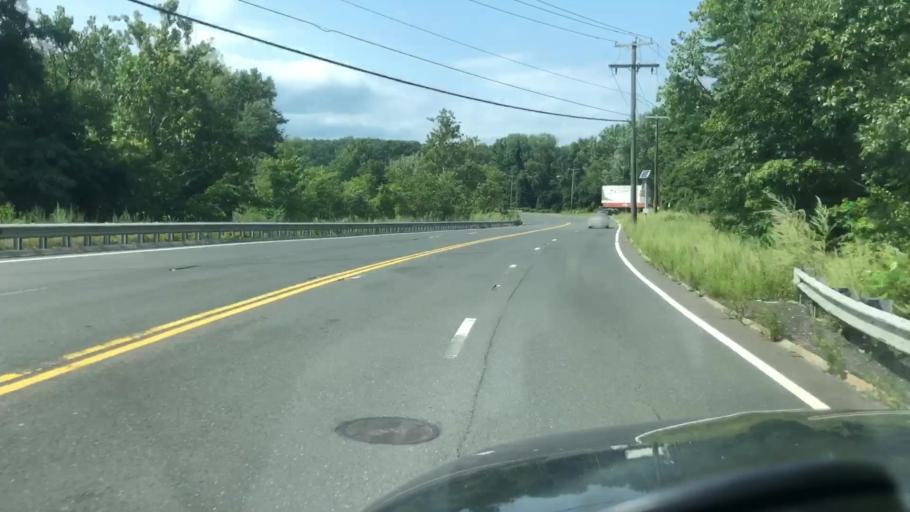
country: US
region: Massachusetts
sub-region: Hampden County
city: West Springfield
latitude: 42.1056
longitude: -72.6817
